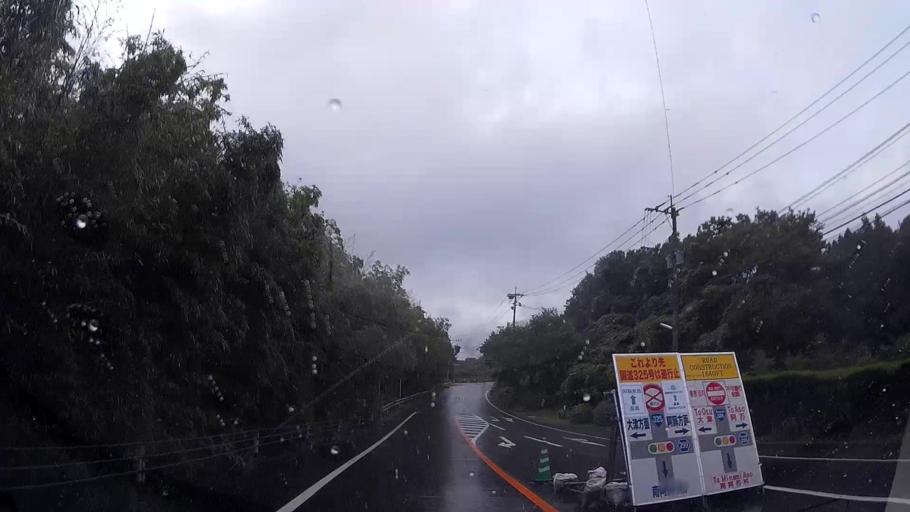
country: JP
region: Kumamoto
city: Aso
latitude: 32.8711
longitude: 130.9946
